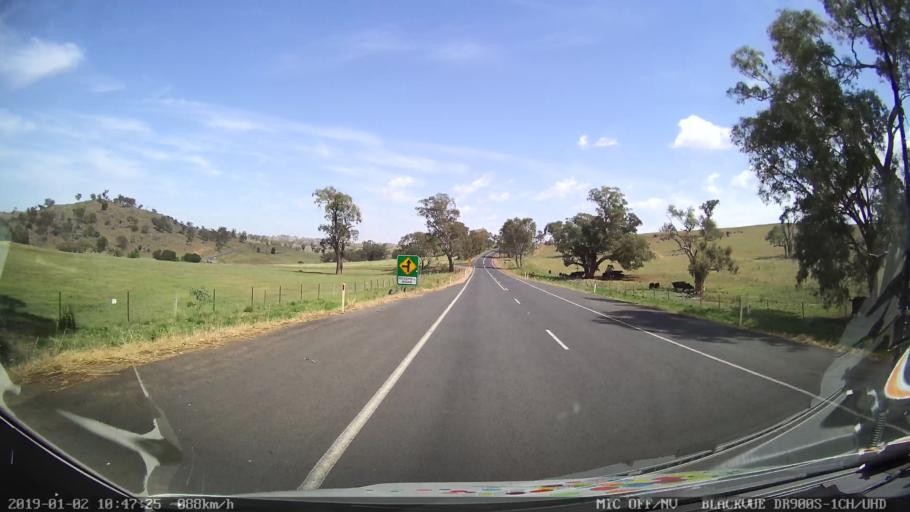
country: AU
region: New South Wales
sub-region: Cootamundra
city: Cootamundra
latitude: -34.7454
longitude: 148.2737
